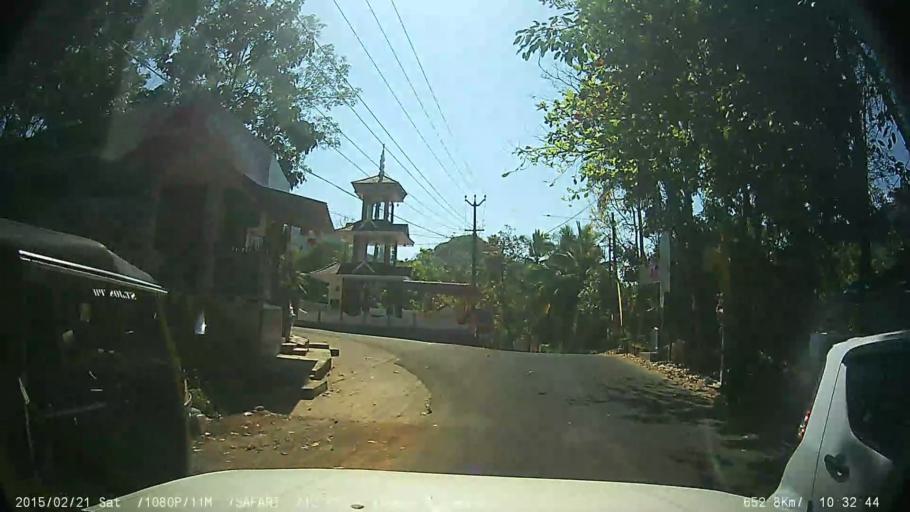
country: IN
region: Kerala
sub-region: Kottayam
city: Lalam
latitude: 9.8385
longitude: 76.7117
